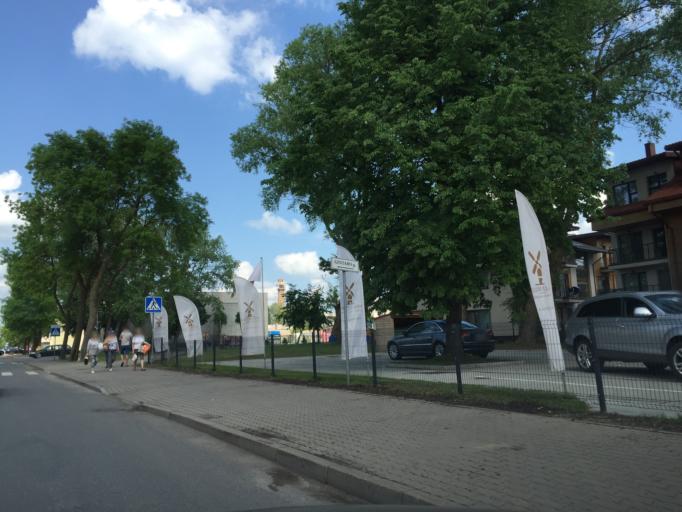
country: LT
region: Klaipedos apskritis
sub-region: Klaipeda
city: Palanga
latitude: 55.9205
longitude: 21.0731
